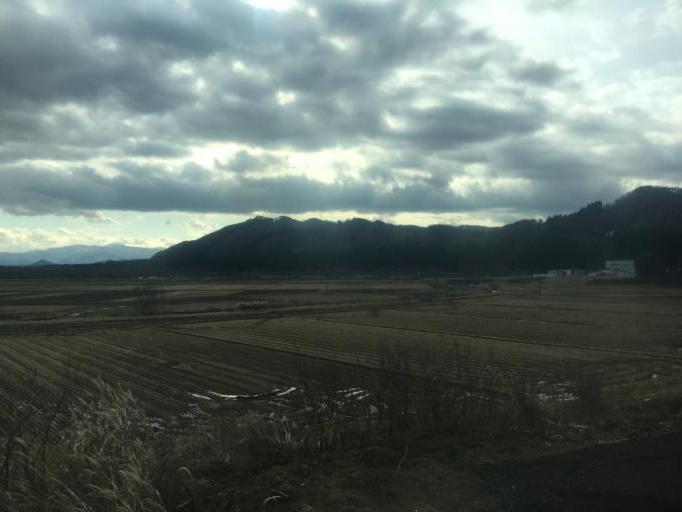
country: JP
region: Akita
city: Odate
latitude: 40.2732
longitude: 140.4735
